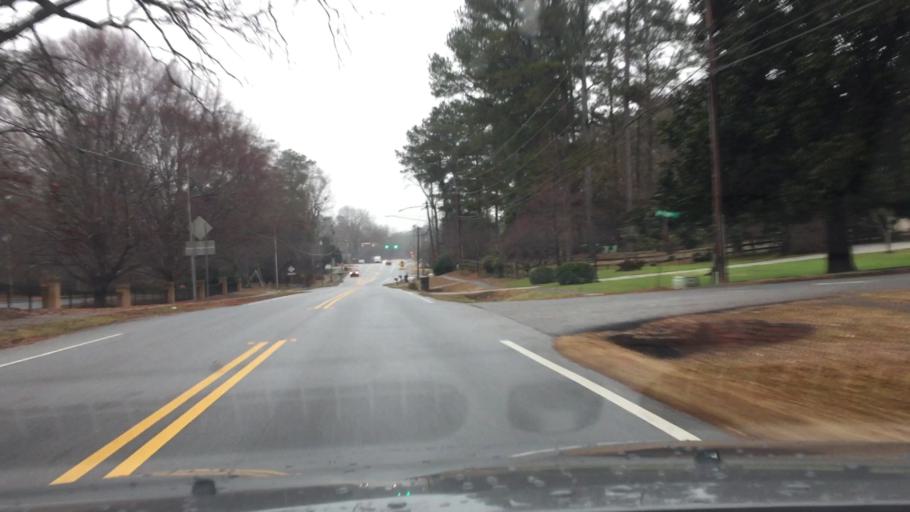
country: US
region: Georgia
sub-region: Cobb County
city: Powder Springs
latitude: 33.8705
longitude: -84.6759
